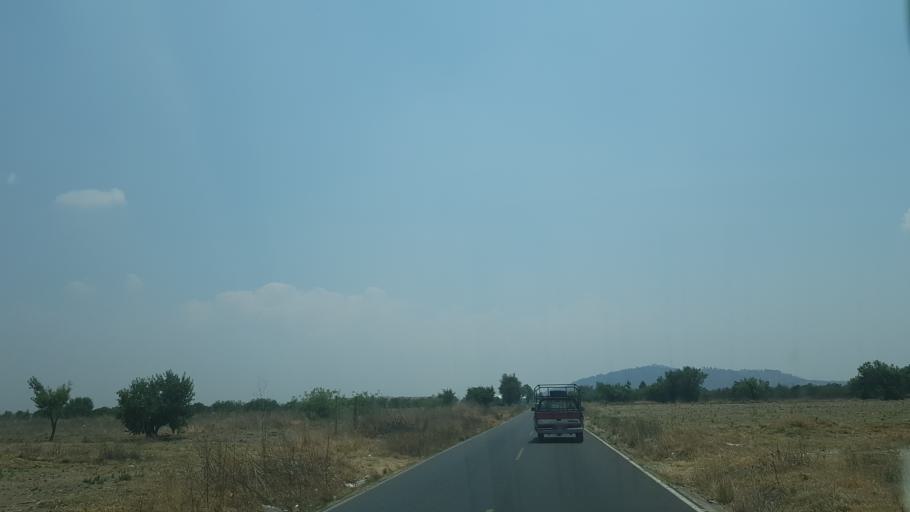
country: MX
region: Puebla
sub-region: San Jeronimo Tecuanipan
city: San Miguel Papaxtla
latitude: 19.0923
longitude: -98.3923
